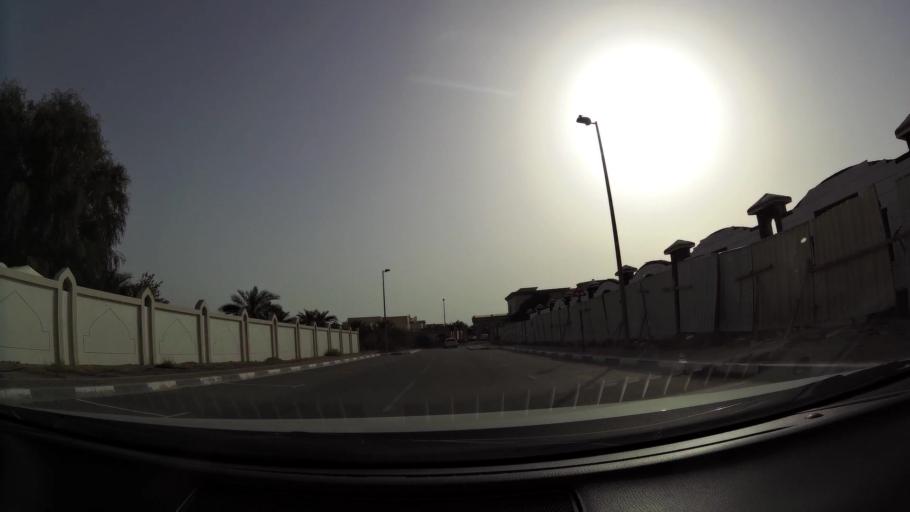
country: AE
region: Abu Dhabi
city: Al Ain
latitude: 24.1236
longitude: 55.6954
